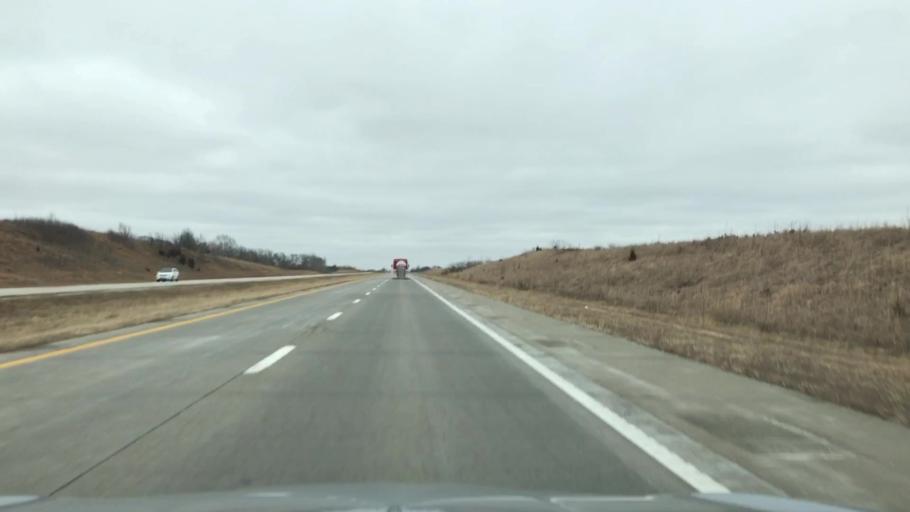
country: US
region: Missouri
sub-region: Caldwell County
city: Hamilton
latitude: 39.7345
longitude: -93.9583
